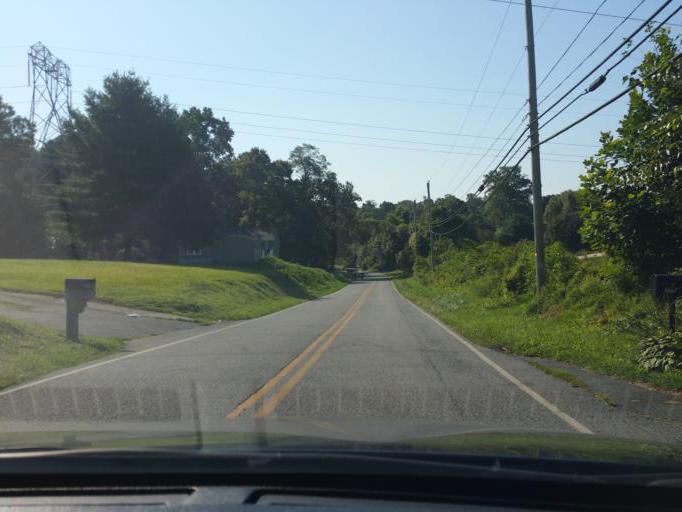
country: US
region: Maryland
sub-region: Cecil County
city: Rising Sun
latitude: 39.6685
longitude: -76.1537
